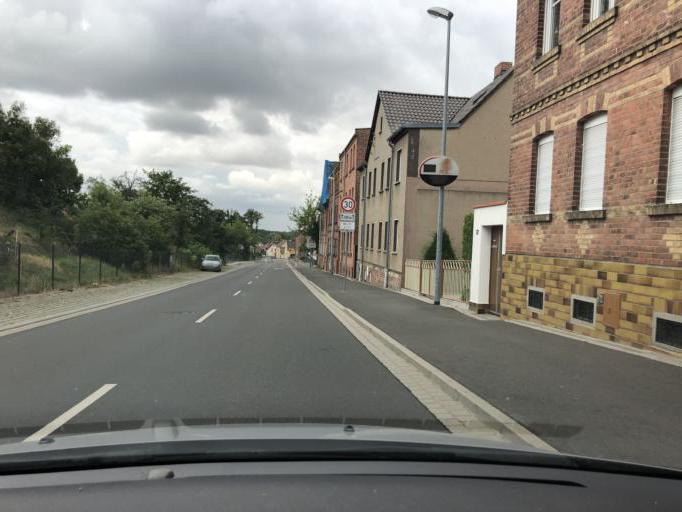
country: DE
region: Saxony-Anhalt
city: Ermlitz
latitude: 51.3935
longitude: 12.1895
